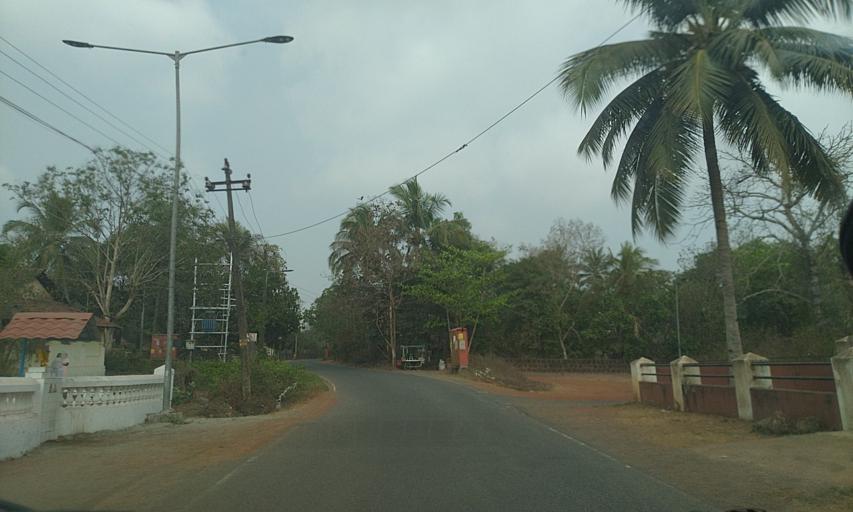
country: IN
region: Goa
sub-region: South Goa
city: Raia
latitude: 15.3075
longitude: 73.9537
